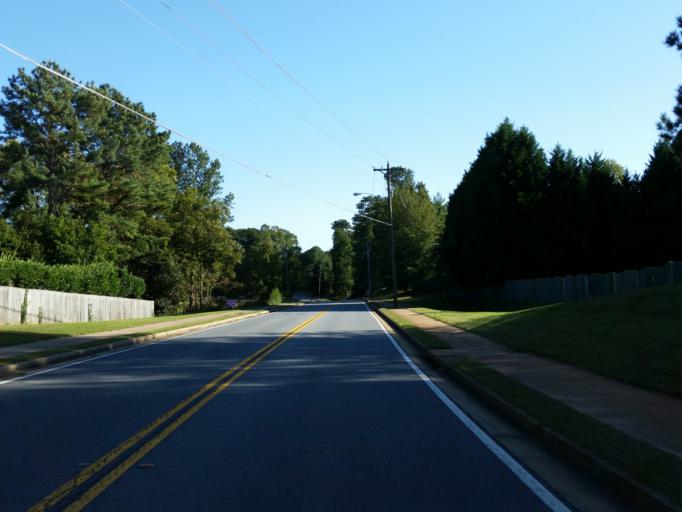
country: US
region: Georgia
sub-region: Cobb County
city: Marietta
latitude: 34.0001
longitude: -84.4721
